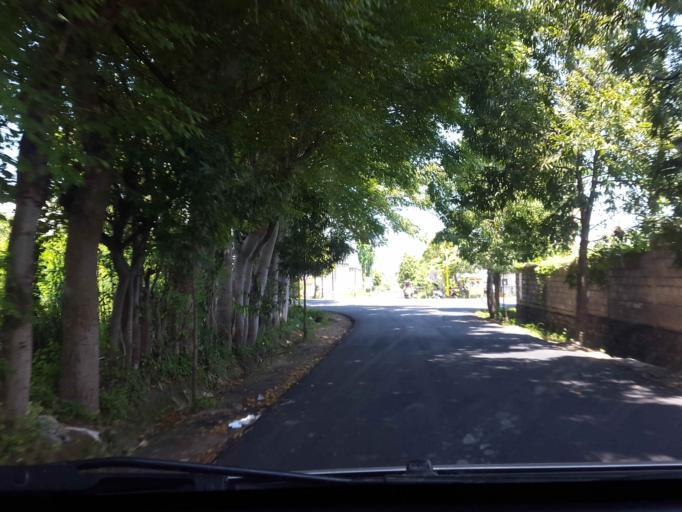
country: ID
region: Bali
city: Semarapura
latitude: -8.5422
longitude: 115.4055
